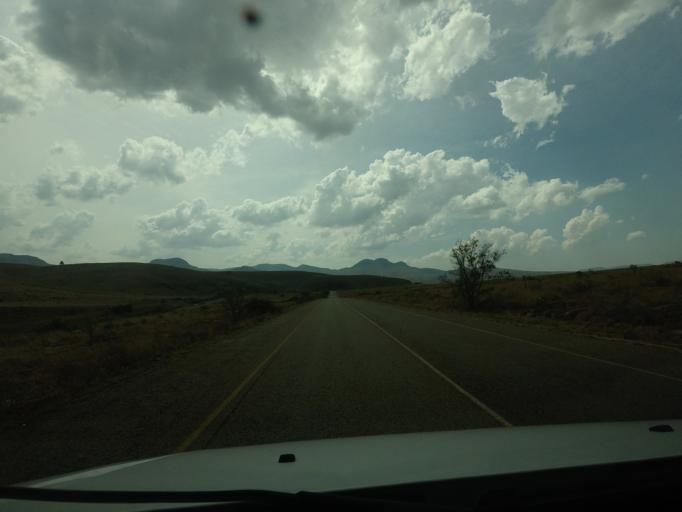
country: ZA
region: Mpumalanga
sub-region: Ehlanzeni District
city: Graksop
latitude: -24.6954
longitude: 30.8179
